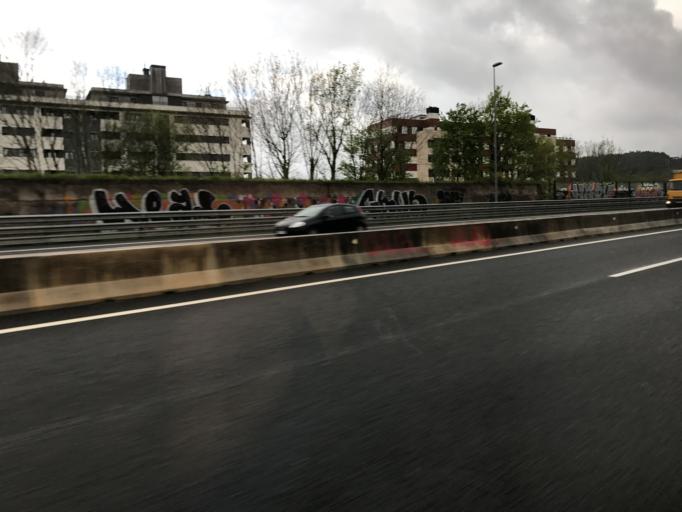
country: ES
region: Basque Country
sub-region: Bizkaia
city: Derio
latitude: 43.3008
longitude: -2.8830
